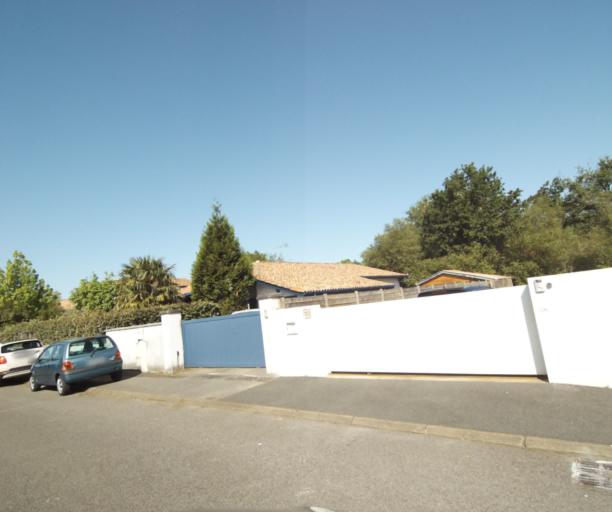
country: FR
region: Aquitaine
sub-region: Departement des Pyrenees-Atlantiques
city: Mouguerre
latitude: 43.4701
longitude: -1.4438
